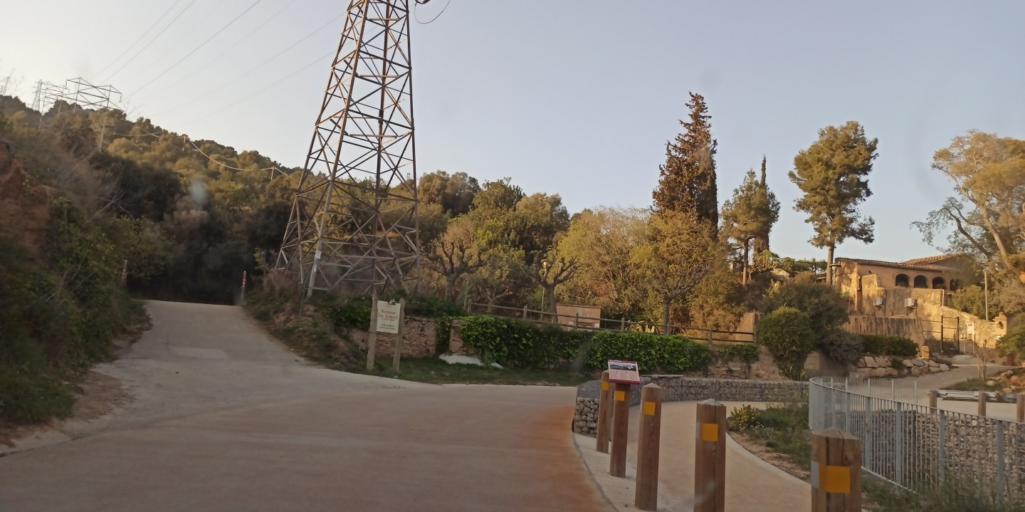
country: ES
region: Catalonia
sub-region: Provincia de Barcelona
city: Sant Just Desvern
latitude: 41.3993
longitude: 2.0856
